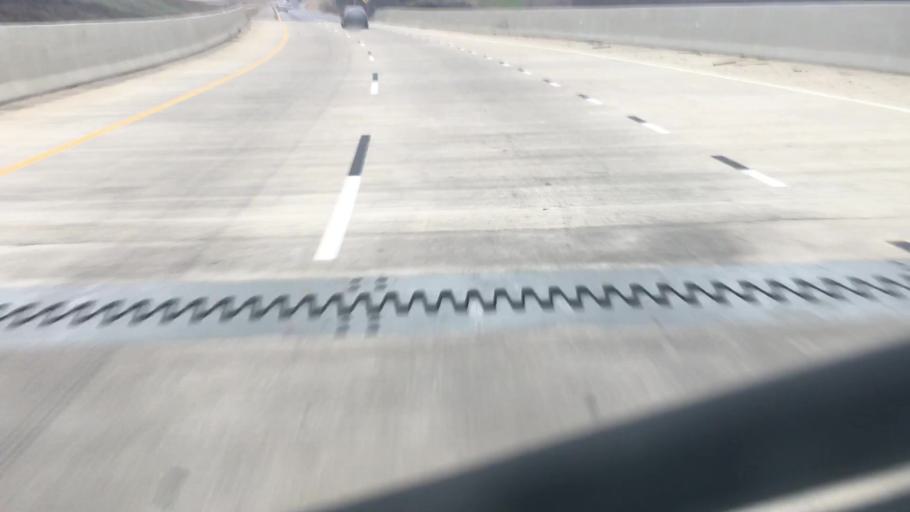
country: US
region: Alabama
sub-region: Jefferson County
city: Fultondale
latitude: 33.5754
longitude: -86.8179
